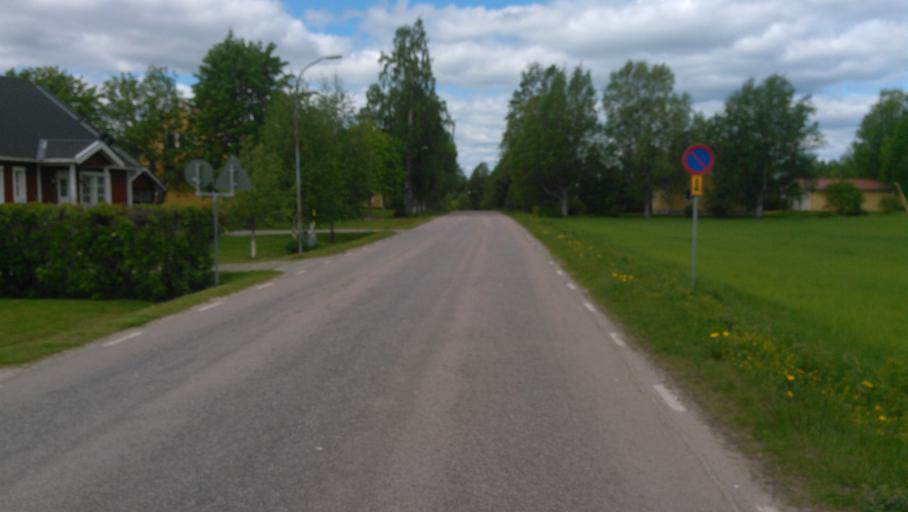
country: SE
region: Vaesterbotten
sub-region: Umea Kommun
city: Roback
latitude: 63.8686
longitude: 20.0706
